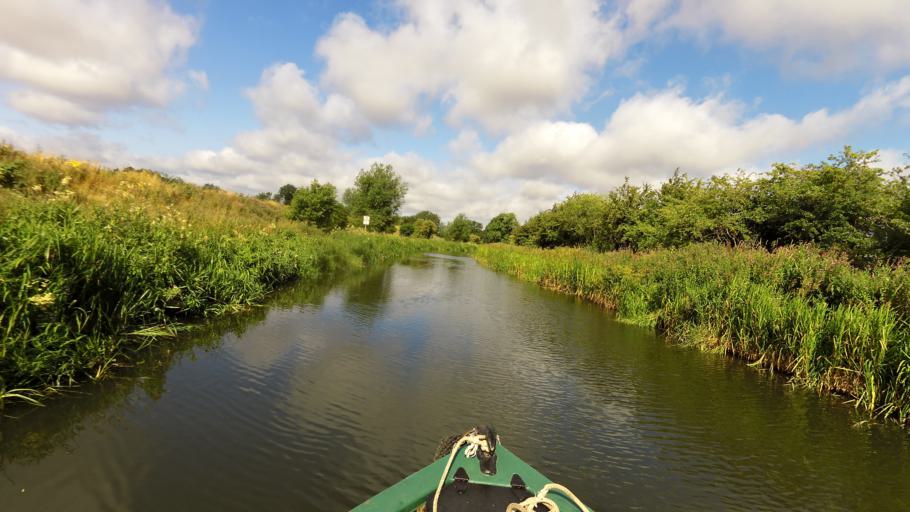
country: GB
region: England
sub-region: West Berkshire
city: Thatcham
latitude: 51.3923
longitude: -1.2168
